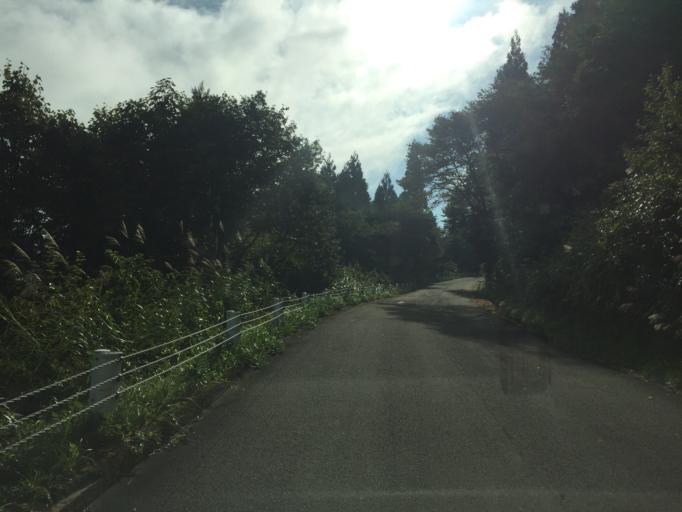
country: JP
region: Fukushima
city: Inawashiro
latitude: 37.4860
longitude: 139.9770
